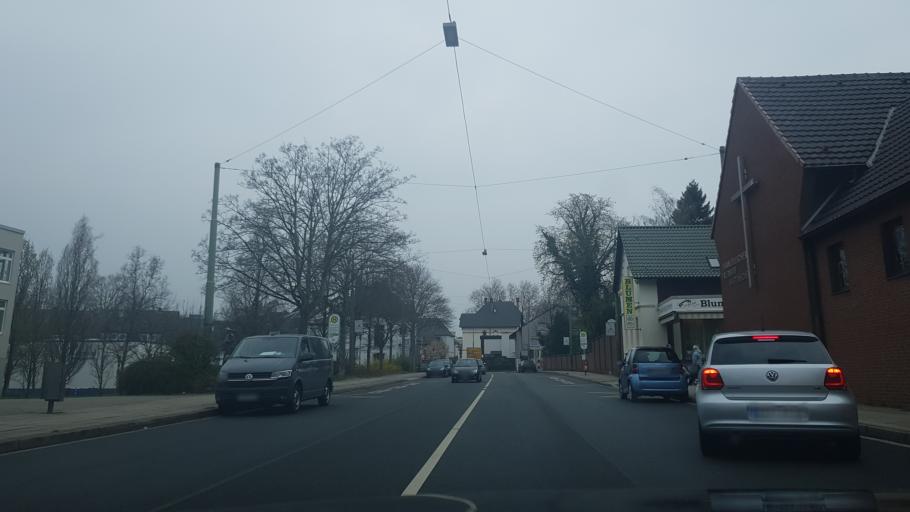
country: DE
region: North Rhine-Westphalia
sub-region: Regierungsbezirk Munster
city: Gelsenkirchen
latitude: 51.4760
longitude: 7.1452
